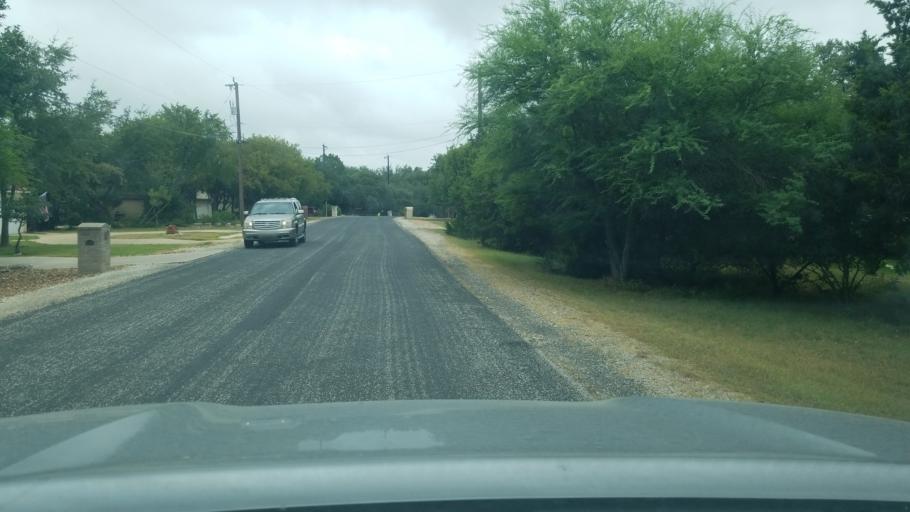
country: US
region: Texas
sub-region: Bexar County
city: Timberwood Park
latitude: 29.7038
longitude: -98.5096
